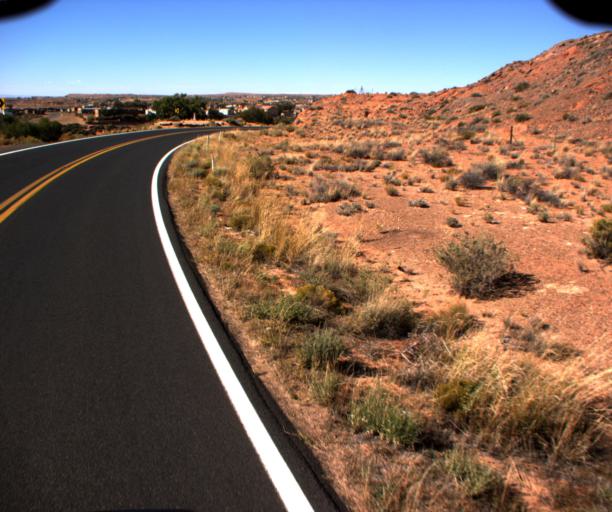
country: US
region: Arizona
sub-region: Coconino County
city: Tuba City
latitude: 36.1082
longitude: -111.2173
